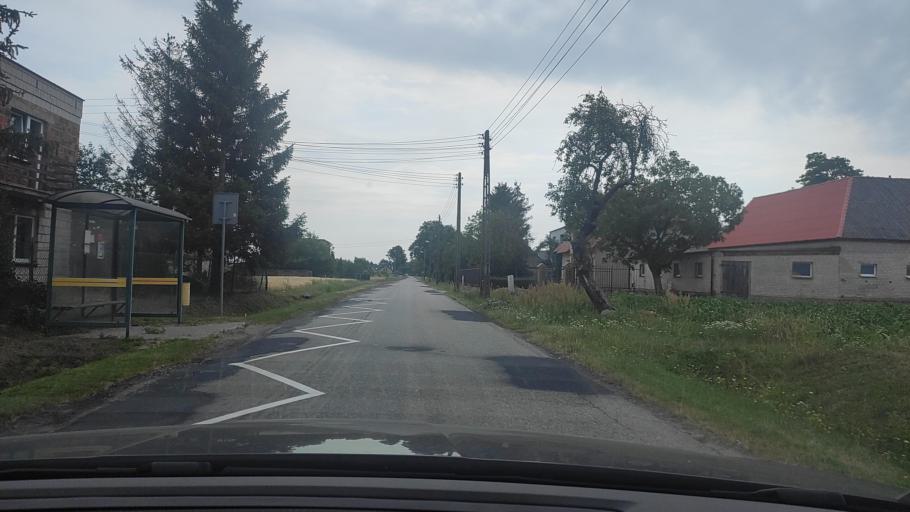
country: PL
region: Greater Poland Voivodeship
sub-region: Powiat poznanski
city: Kleszczewo
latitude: 52.2969
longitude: 17.1389
